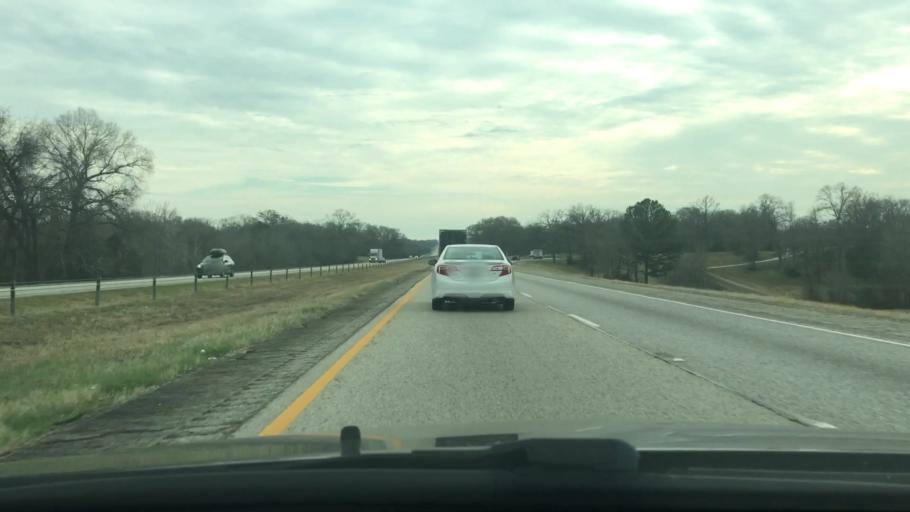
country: US
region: Texas
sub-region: Leon County
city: Centerville
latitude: 31.1987
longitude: -95.9943
